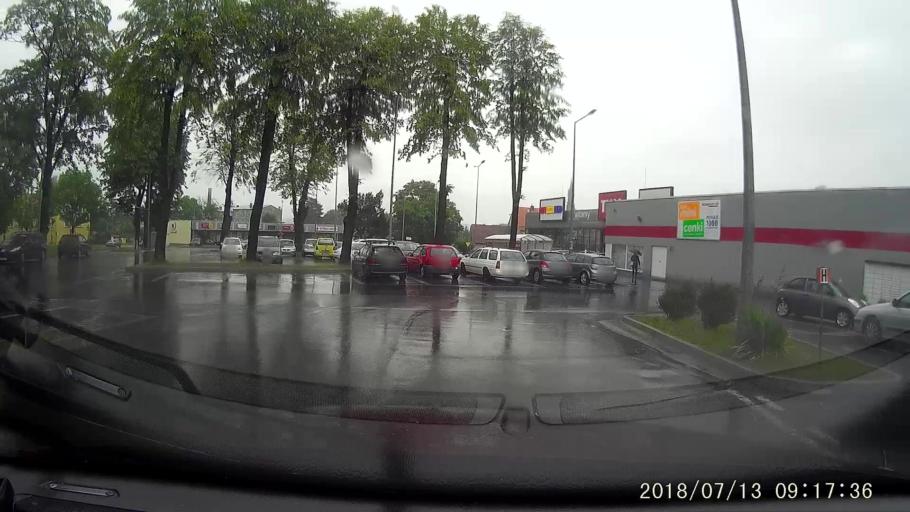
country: PL
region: Lower Silesian Voivodeship
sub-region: Powiat lubanski
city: Luban
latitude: 51.1244
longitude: 15.2869
